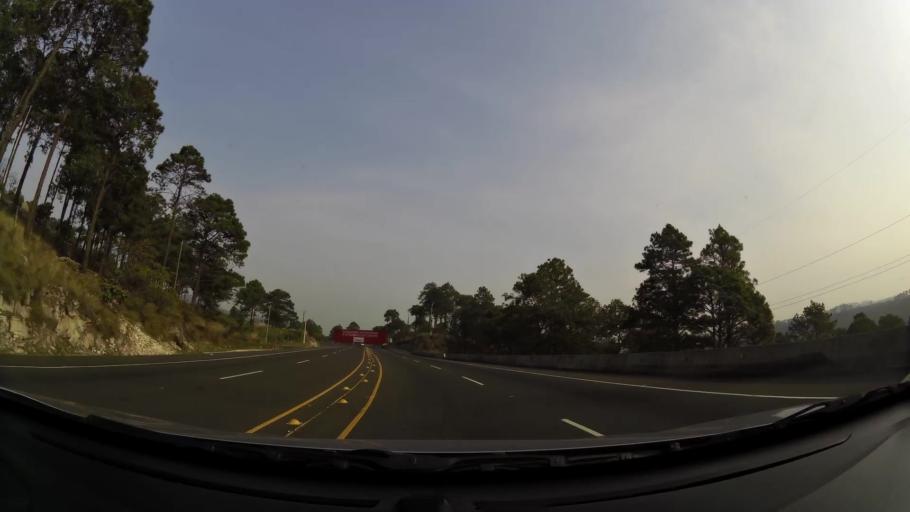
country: HN
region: Francisco Morazan
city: Zambrano
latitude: 14.2510
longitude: -87.3760
